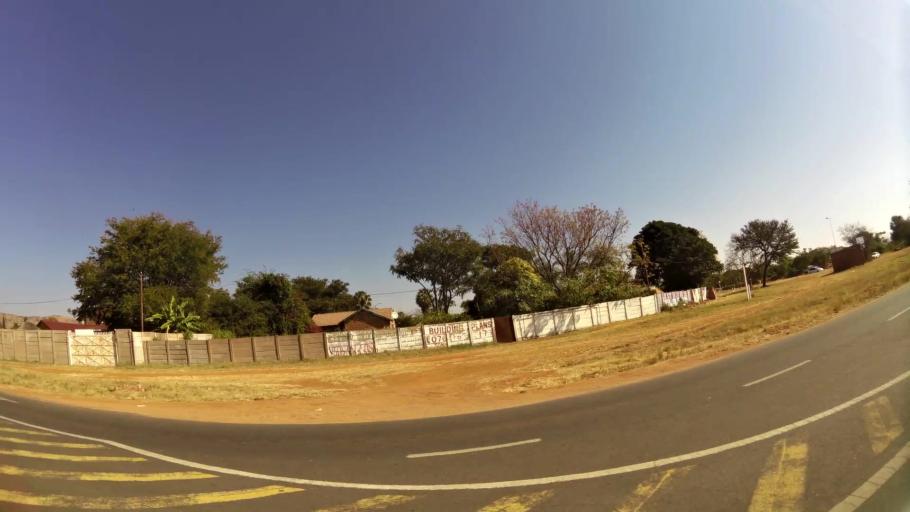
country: ZA
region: North-West
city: Ga-Rankuwa
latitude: -25.6636
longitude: 28.1015
